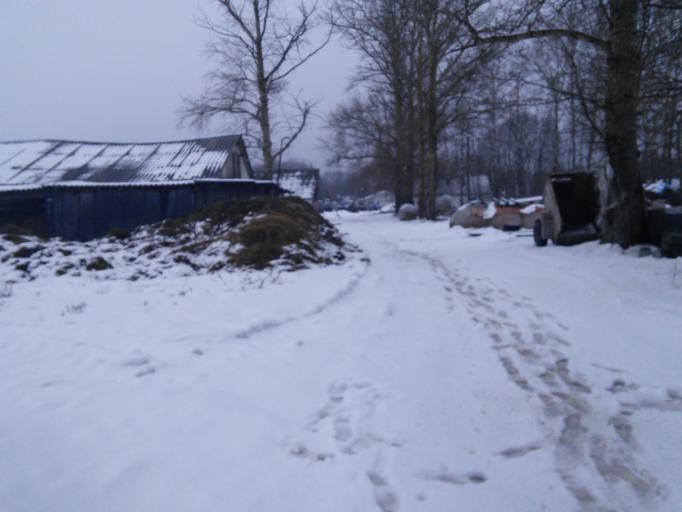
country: RU
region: Kursk
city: Chernitsyno
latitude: 51.5713
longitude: 36.0857
